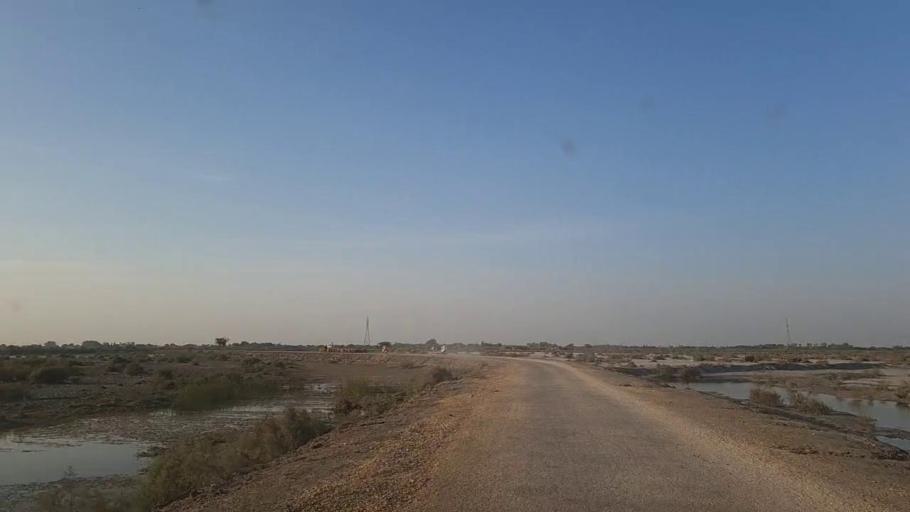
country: PK
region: Sindh
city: Mirpur Batoro
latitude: 24.6895
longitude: 68.2028
